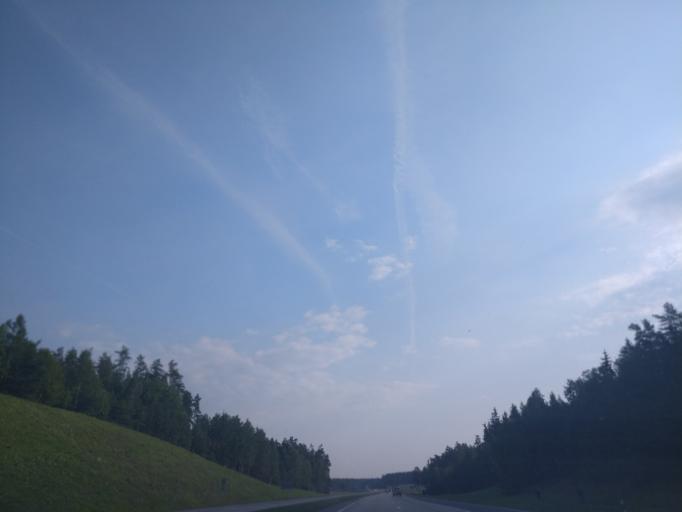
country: BY
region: Minsk
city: Borovlyany
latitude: 54.0296
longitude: 27.6777
